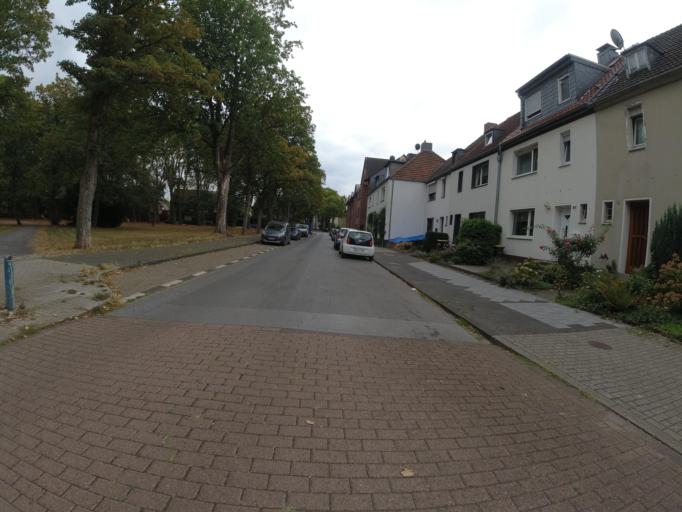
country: DE
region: North Rhine-Westphalia
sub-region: Regierungsbezirk Dusseldorf
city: Hochfeld
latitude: 51.4560
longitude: 6.6992
